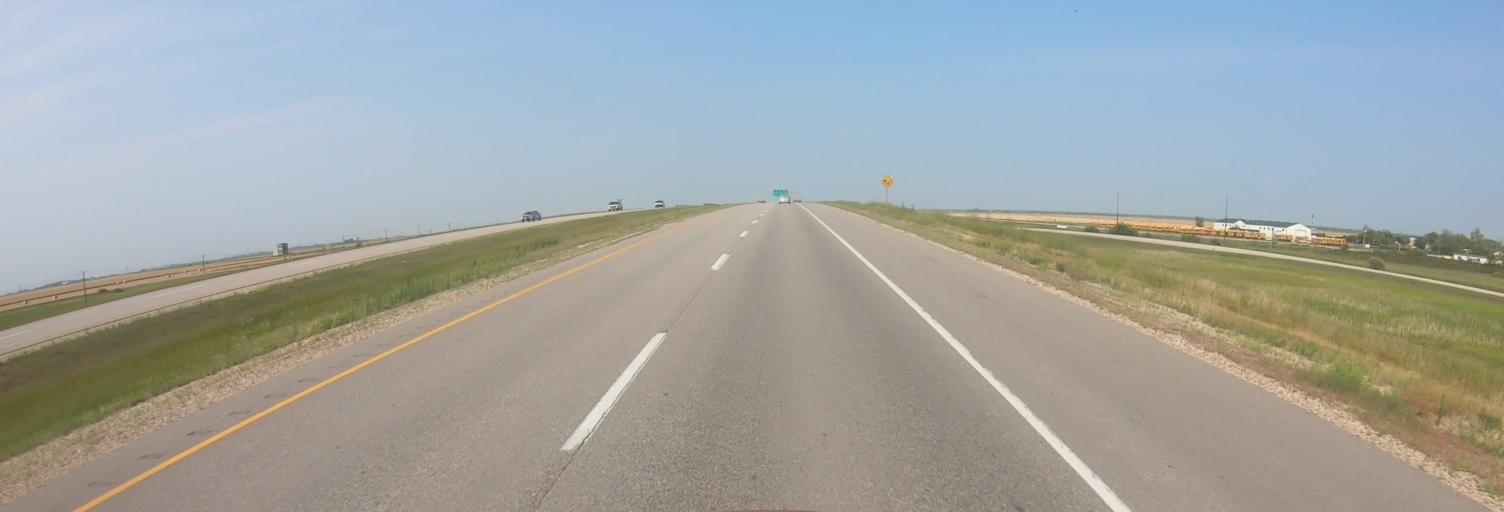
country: CA
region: Manitoba
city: Steinbach
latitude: 49.6750
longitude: -96.6671
